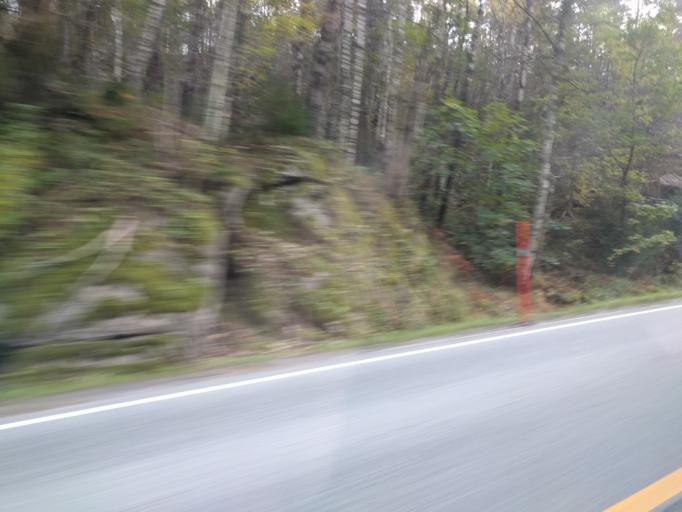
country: NO
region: Vest-Agder
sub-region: Songdalen
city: Nodeland
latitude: 58.2585
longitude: 7.8369
